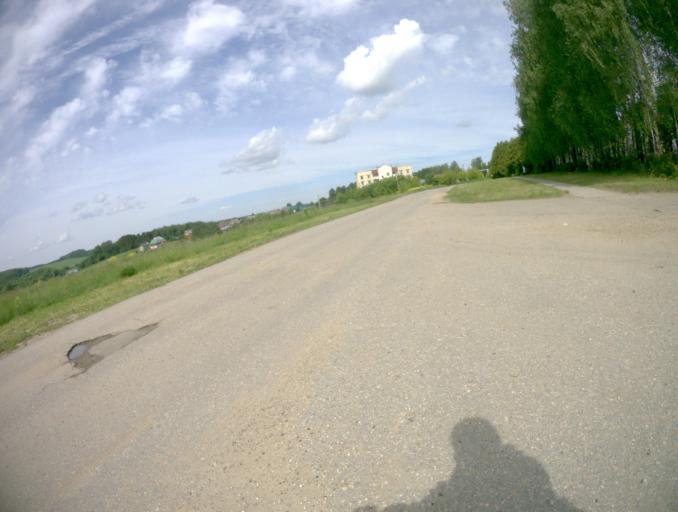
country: RU
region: Vladimir
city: Stavrovo
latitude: 56.0918
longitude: 39.9728
